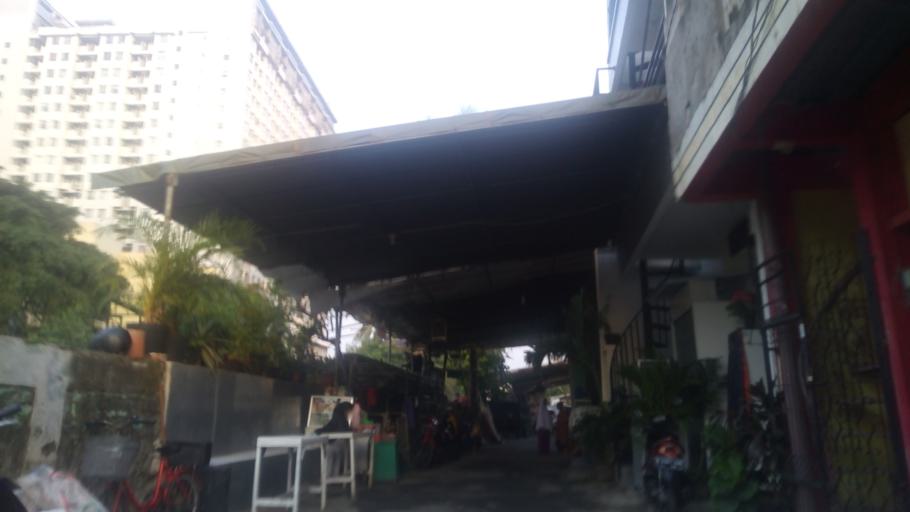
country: ID
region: Jakarta Raya
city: Jakarta
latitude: -6.2003
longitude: 106.8499
